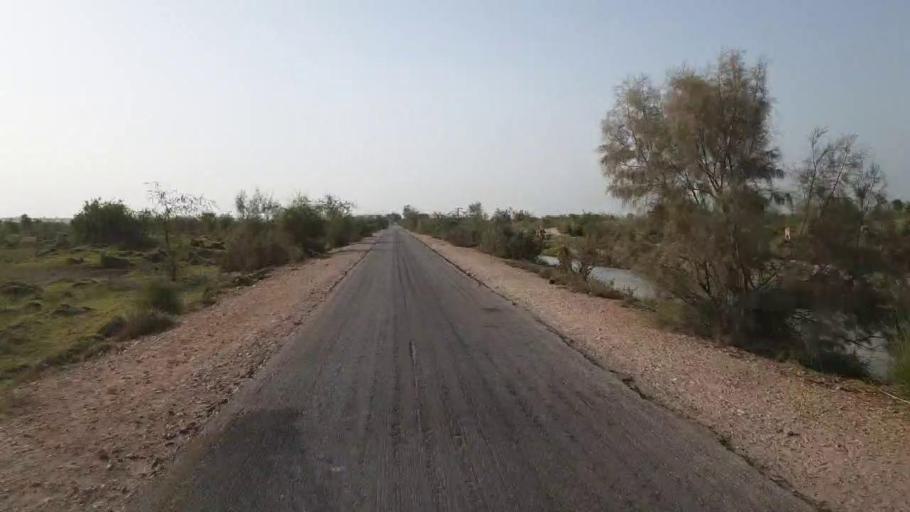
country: PK
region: Sindh
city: Jam Sahib
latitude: 26.4555
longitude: 68.8607
